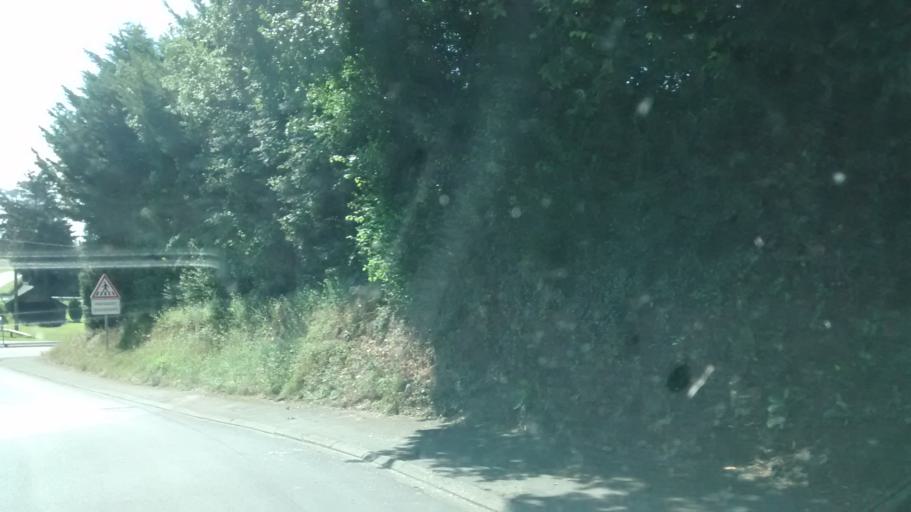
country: FR
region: Brittany
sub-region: Departement du Morbihan
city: Campeneac
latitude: 47.9568
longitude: -2.2926
